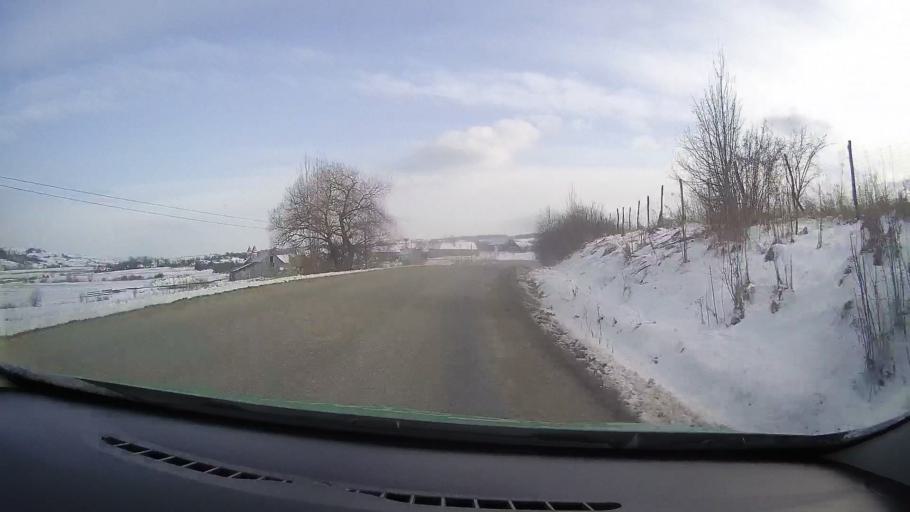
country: RO
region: Sibiu
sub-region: Comuna Merghindeal
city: Merghindeal
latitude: 45.9689
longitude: 24.7114
